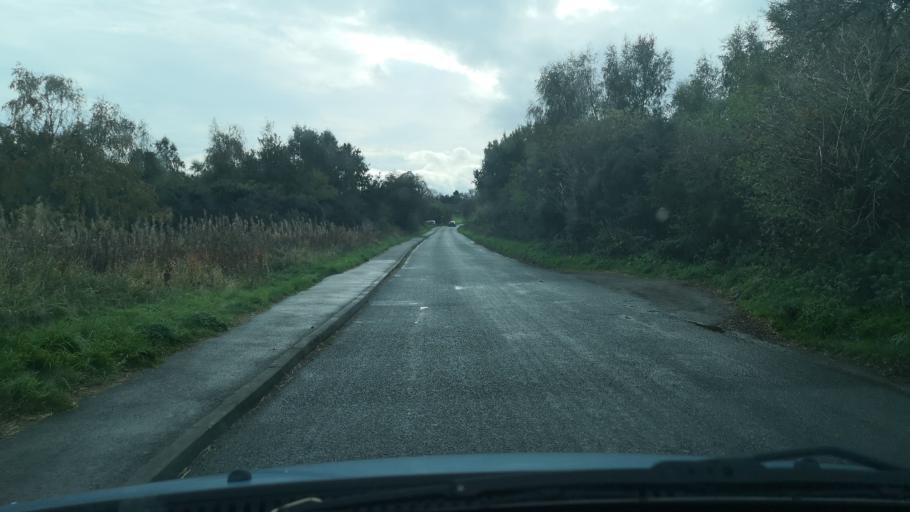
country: GB
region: England
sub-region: City and Borough of Wakefield
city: Sharlston
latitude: 53.6686
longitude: -1.4066
